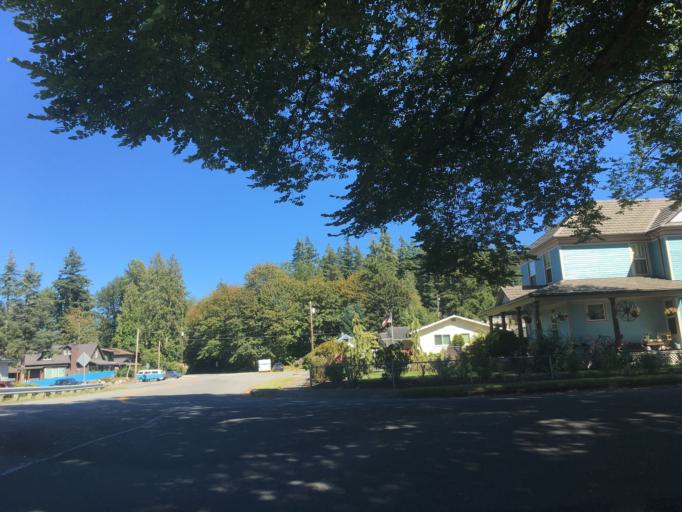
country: US
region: Washington
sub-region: Snohomish County
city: Arlington
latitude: 48.1984
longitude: -122.1227
